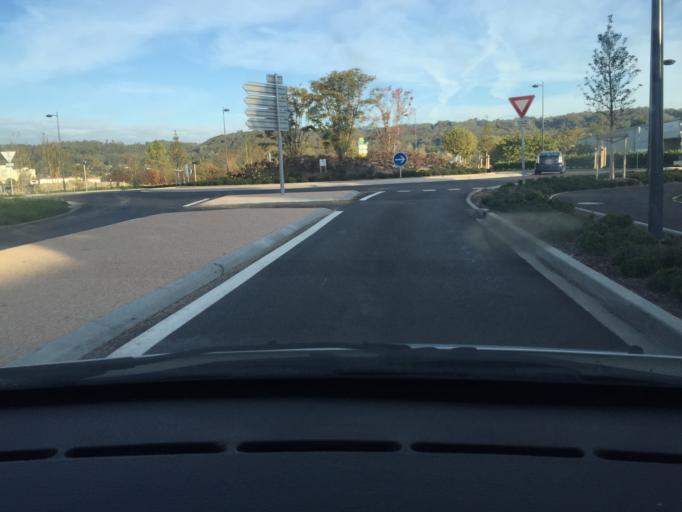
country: FR
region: Rhone-Alpes
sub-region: Departement de l'Ain
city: Beynost
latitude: 45.8264
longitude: 4.9937
